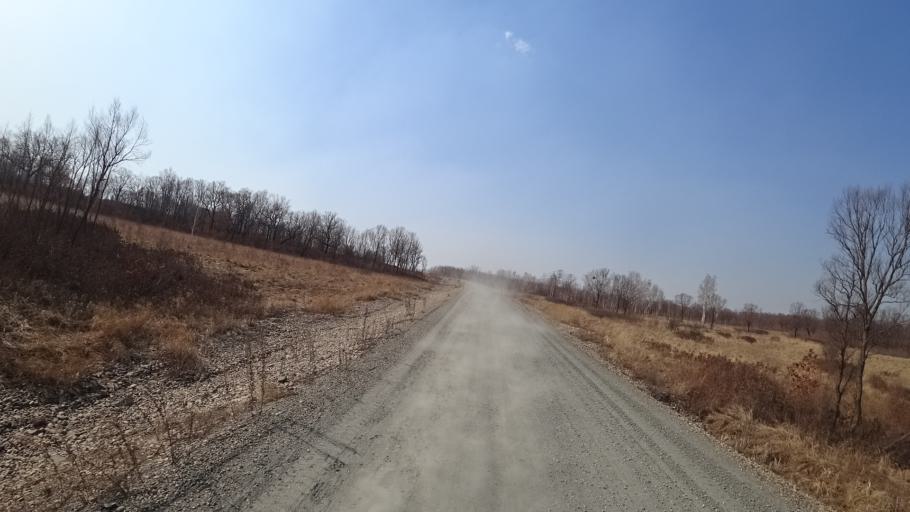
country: RU
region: Amur
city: Novobureyskiy
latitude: 49.8256
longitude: 129.9945
